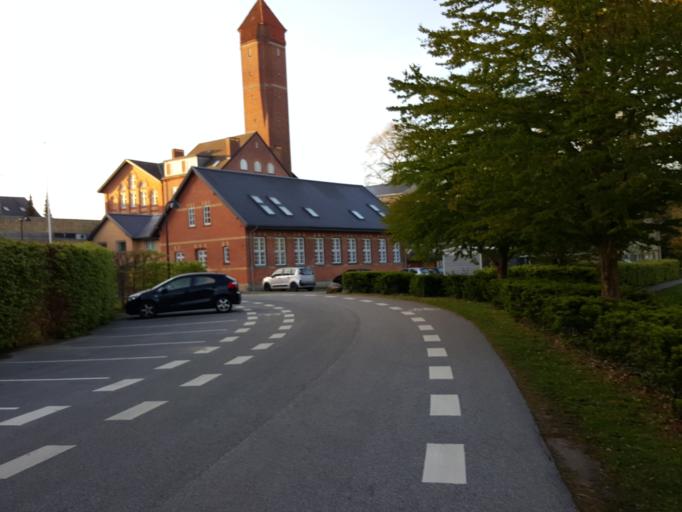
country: DK
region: Capital Region
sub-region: Rudersdal Kommune
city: Holte
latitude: 55.8477
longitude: 12.4601
